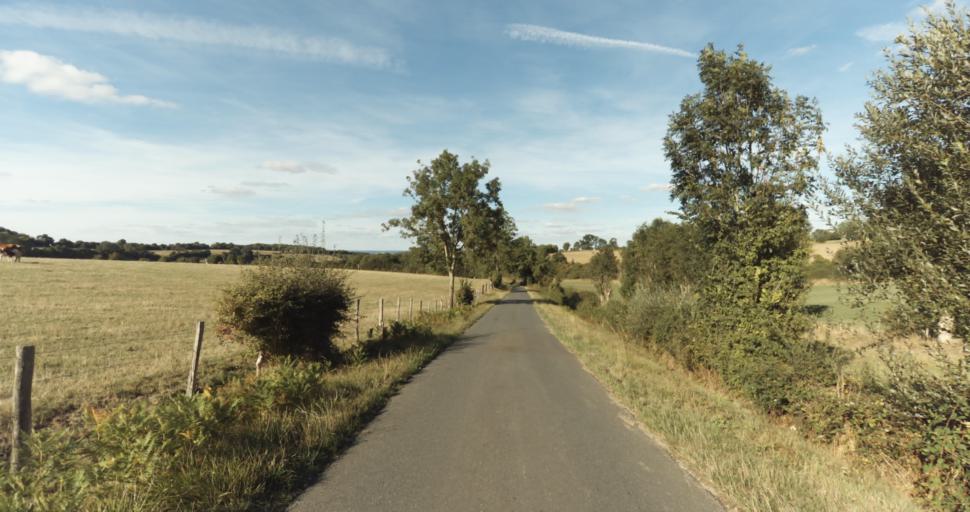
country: FR
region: Lower Normandy
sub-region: Departement de l'Orne
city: Vimoutiers
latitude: 48.9023
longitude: 0.1205
